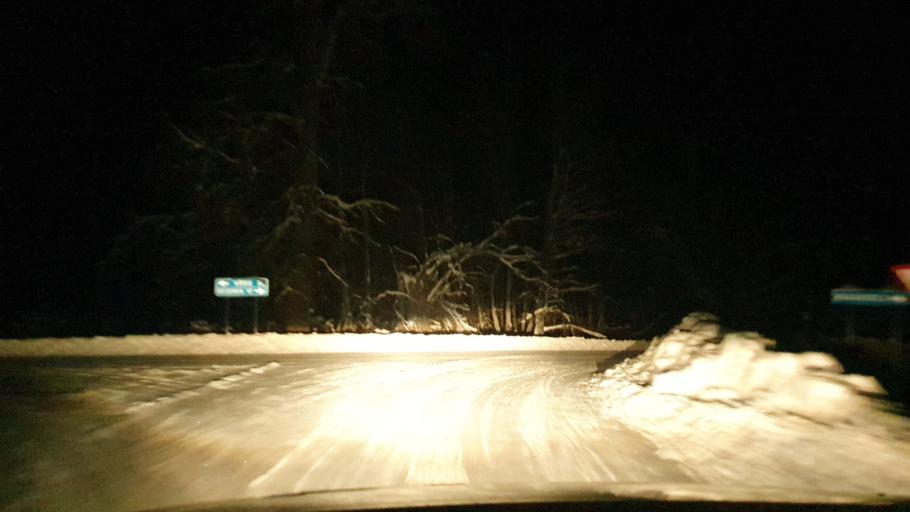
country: EE
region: Vorumaa
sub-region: Antsla vald
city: Vana-Antsla
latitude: 57.9638
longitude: 26.6441
